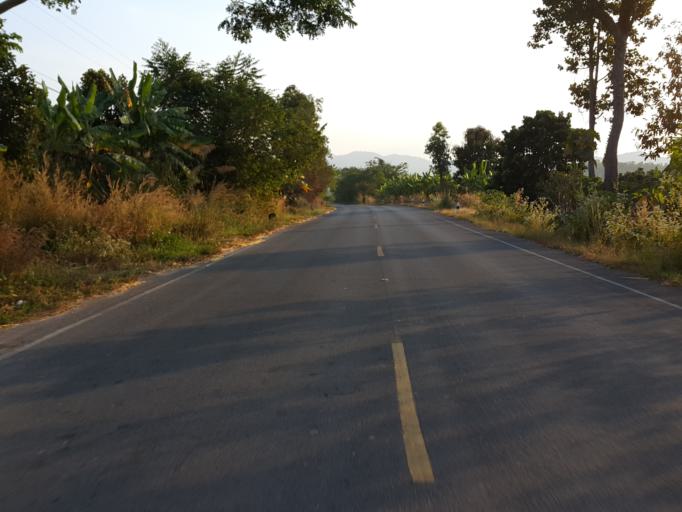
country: TH
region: Lamphun
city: Thung Hua Chang
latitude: 17.8903
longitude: 99.0610
